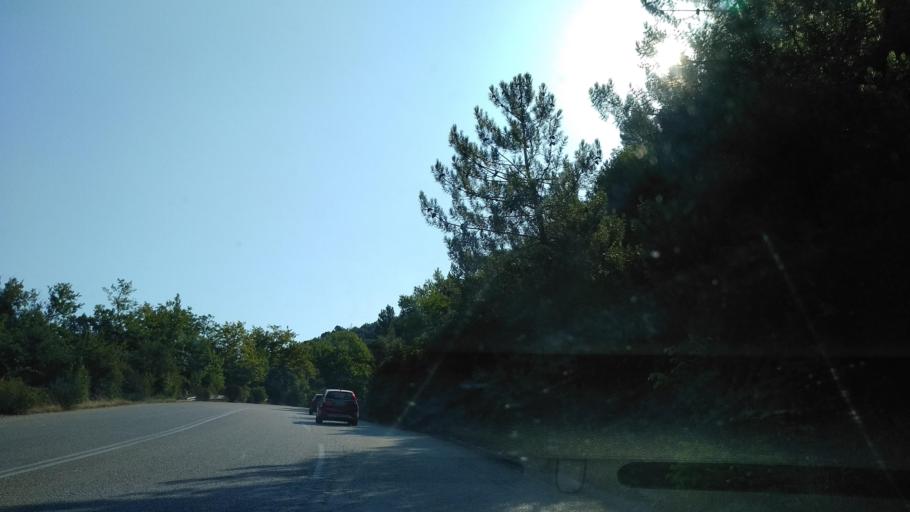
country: GR
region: Central Macedonia
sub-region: Nomos Chalkidikis
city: Stratonion
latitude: 40.5467
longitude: 23.8222
